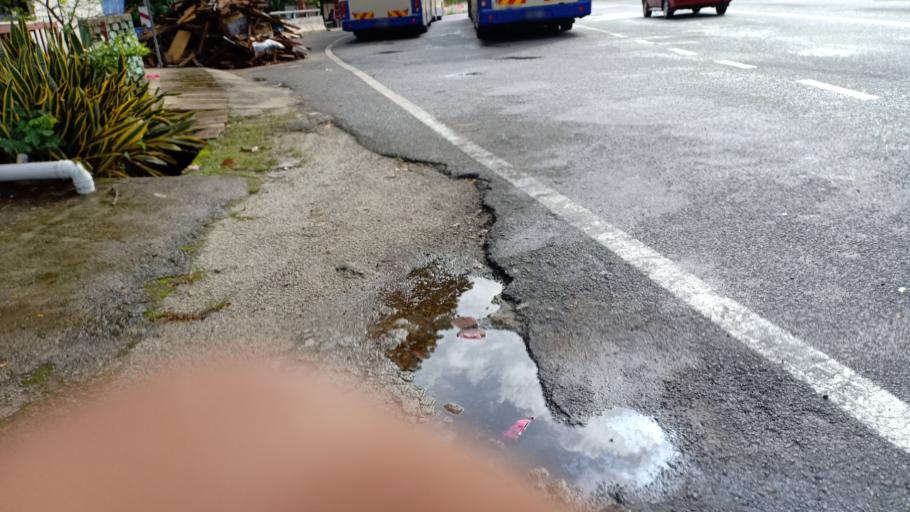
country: MY
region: Penang
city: Tanjung Tokong
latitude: 5.4586
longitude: 100.2158
